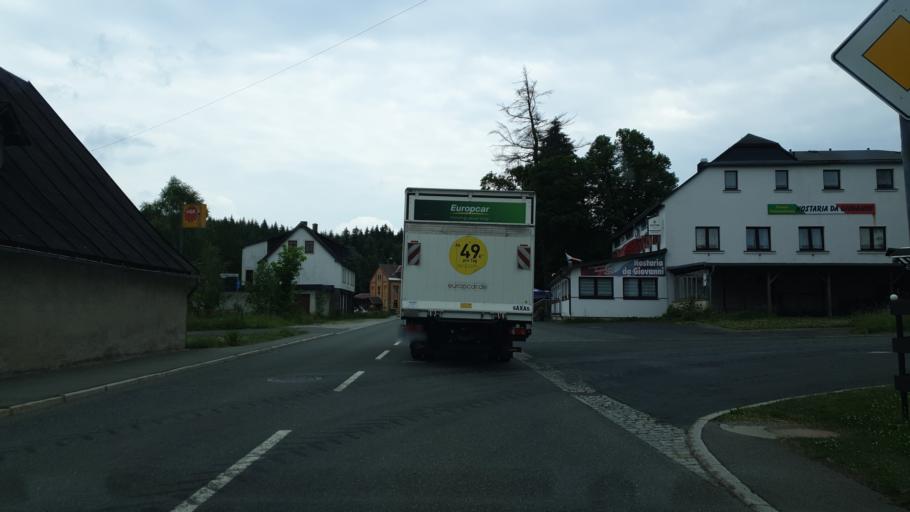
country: DE
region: Saxony
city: Muldenhammer
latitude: 50.4503
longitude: 12.4670
